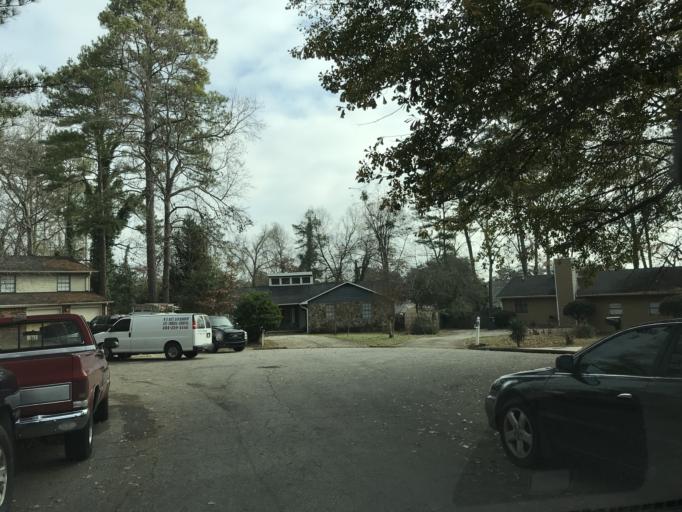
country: US
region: Georgia
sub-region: Clayton County
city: Jonesboro
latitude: 33.5574
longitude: -84.3729
